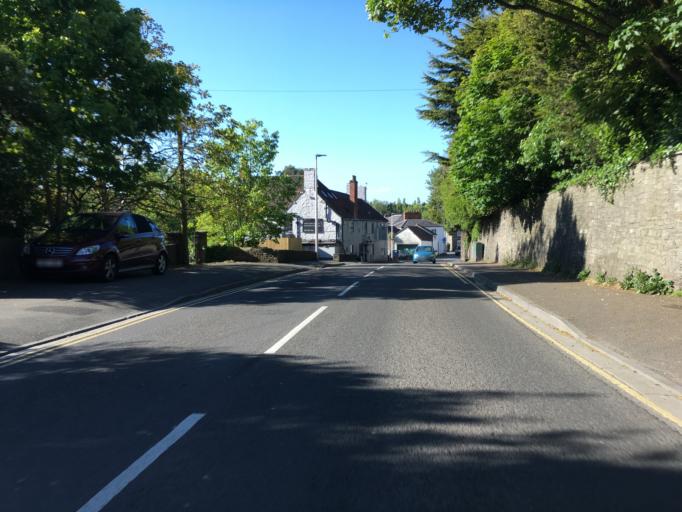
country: GB
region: England
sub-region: North Somerset
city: Clevedon
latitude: 51.4404
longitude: -2.8418
